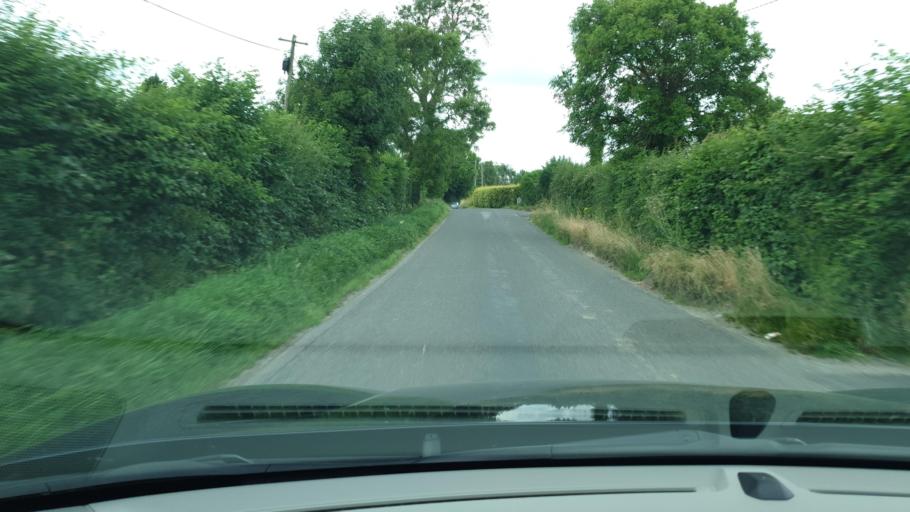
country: IE
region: Leinster
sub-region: An Mhi
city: Ashbourne
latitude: 53.4750
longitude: -6.3749
